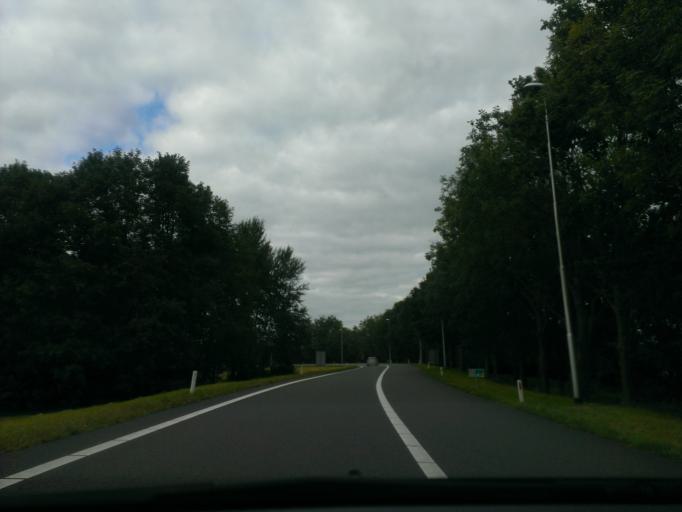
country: NL
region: Gelderland
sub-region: Gemeente Heerde
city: Heerde
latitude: 52.3710
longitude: 6.0249
